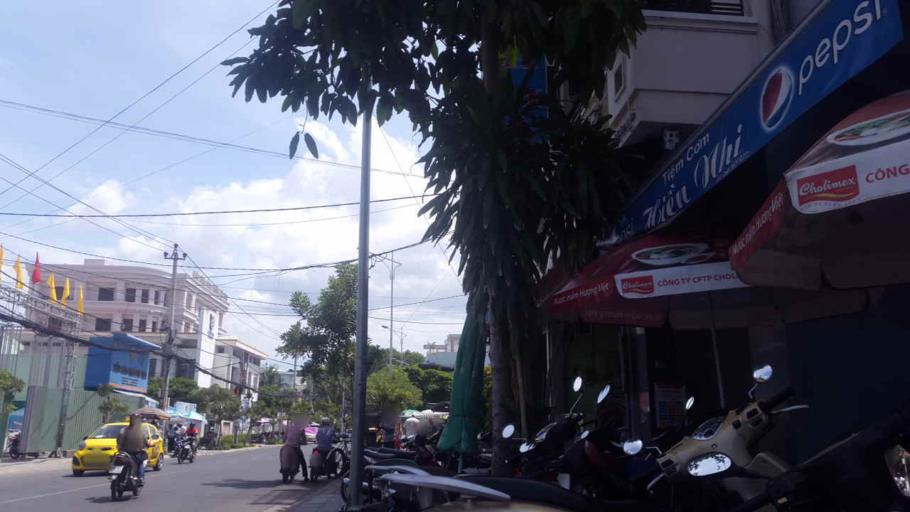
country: VN
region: Khanh Hoa
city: Nha Trang
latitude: 12.2494
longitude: 109.1941
